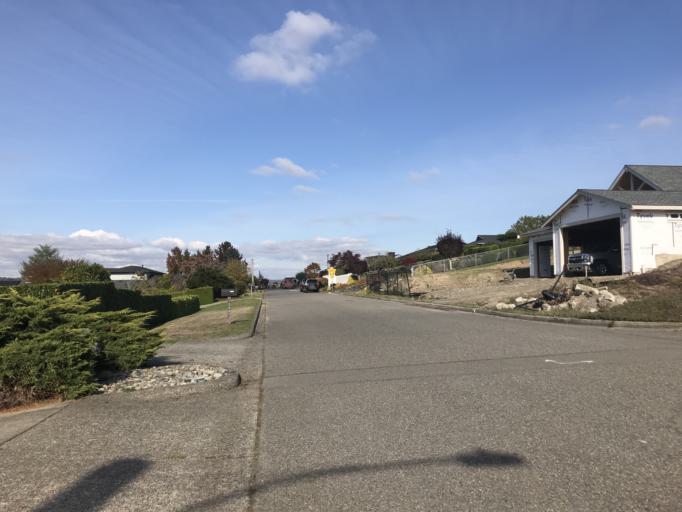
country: US
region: Washington
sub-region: Pierce County
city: University Place
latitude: 47.2446
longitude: -122.5424
